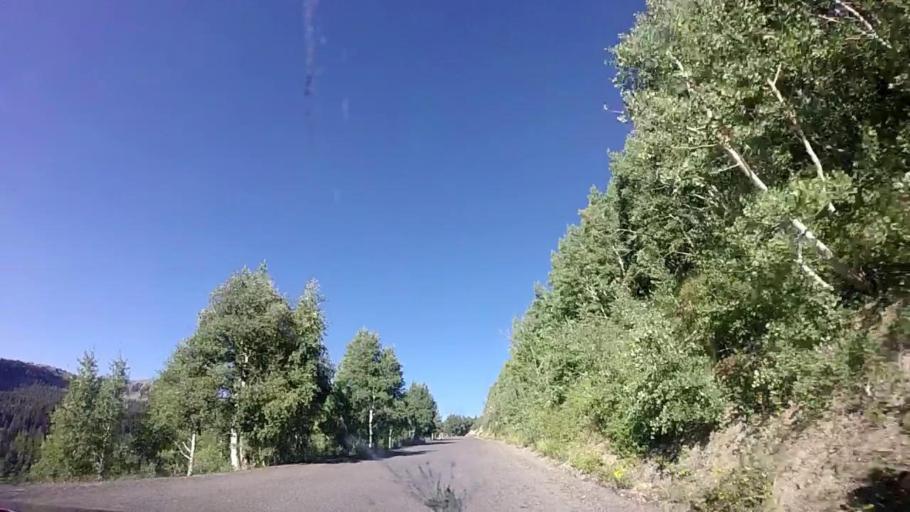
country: US
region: Utah
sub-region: Summit County
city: Park City
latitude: 40.6089
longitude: -111.5451
